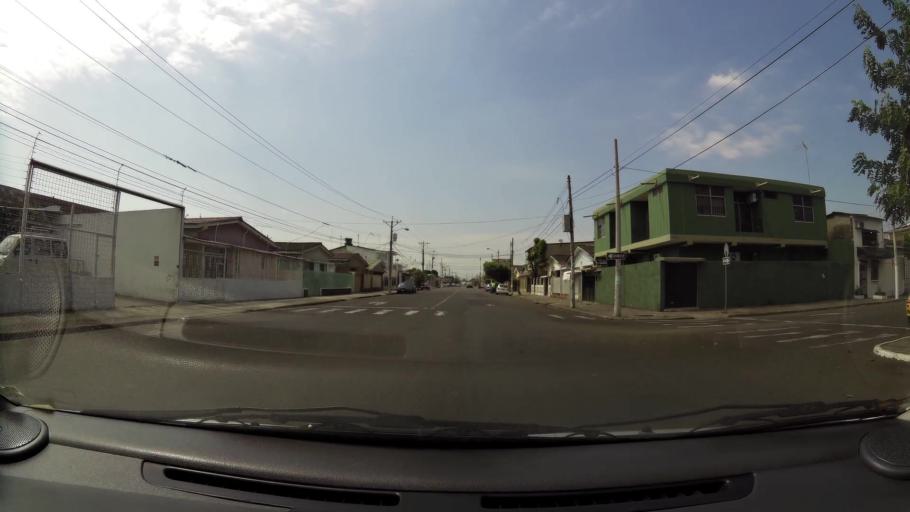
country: EC
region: Guayas
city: Guayaquil
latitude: -2.2314
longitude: -79.8959
